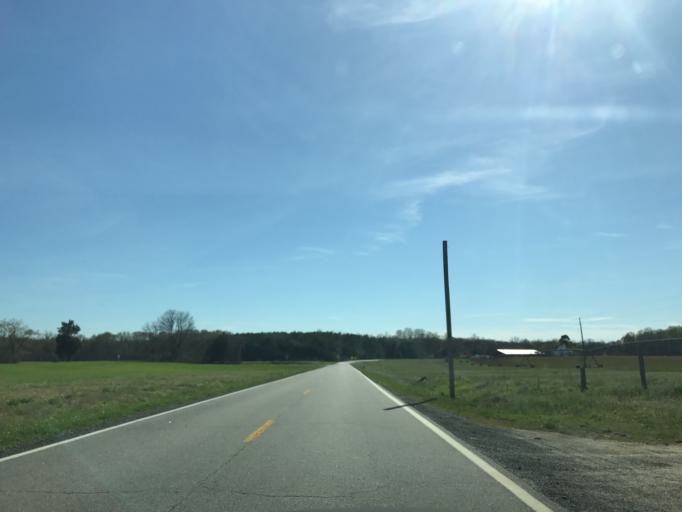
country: US
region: Maryland
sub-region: Caroline County
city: Ridgely
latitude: 38.9792
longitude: -75.9543
